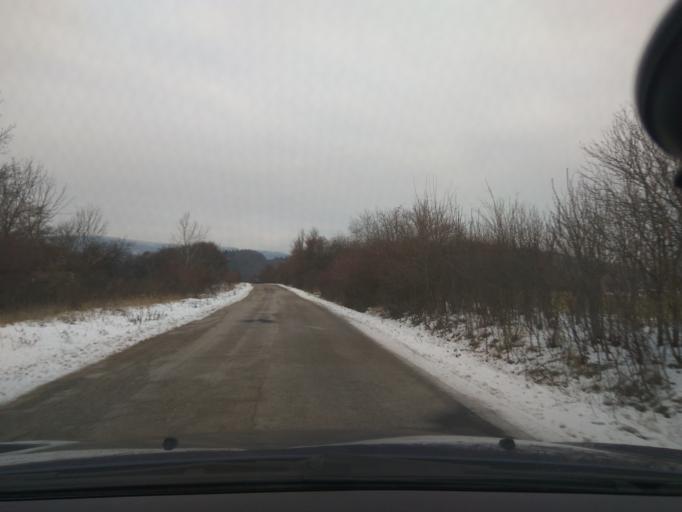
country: SK
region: Nitriansky
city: Stara Tura
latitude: 48.8101
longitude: 17.7095
